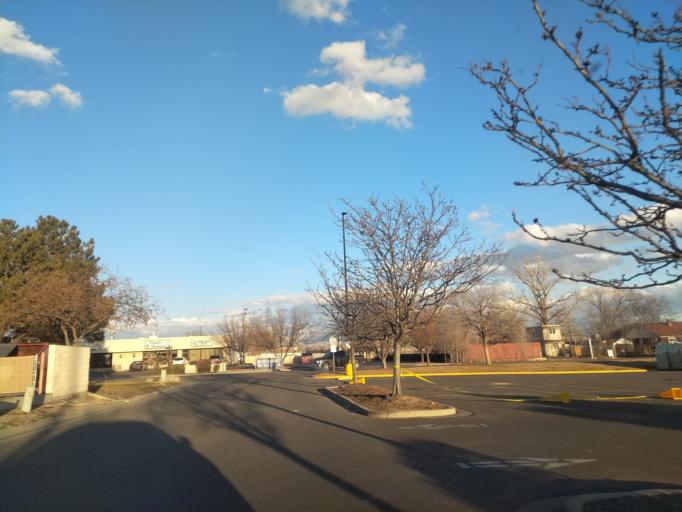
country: US
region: Colorado
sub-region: Mesa County
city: Fruitvale
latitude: 39.0766
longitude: -108.5181
